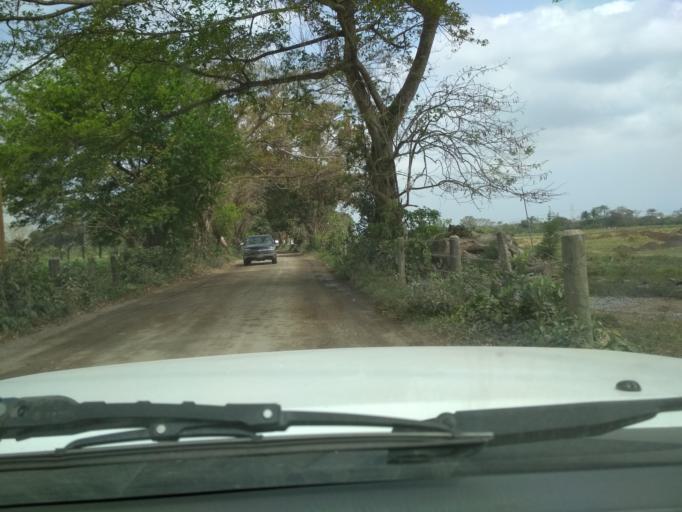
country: MX
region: Veracruz
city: El Tejar
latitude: 19.0862
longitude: -96.1707
